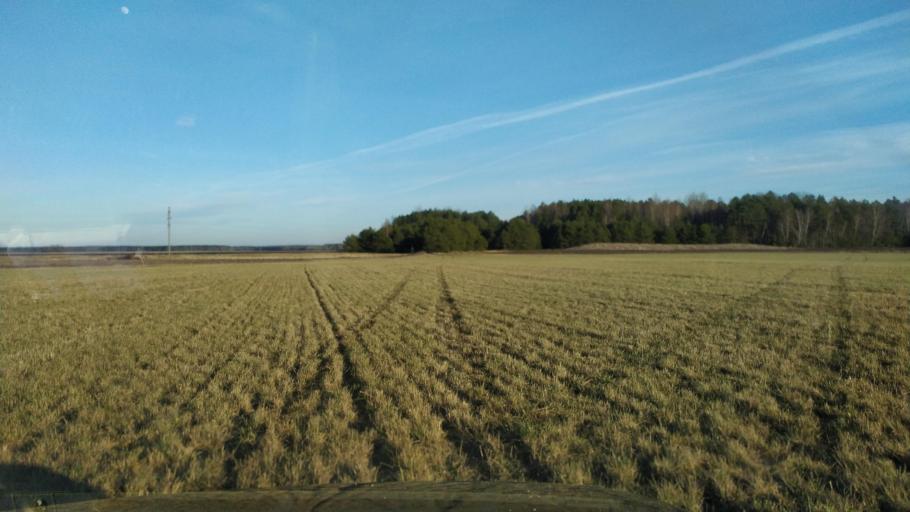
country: BY
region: Brest
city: Pruzhany
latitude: 52.5447
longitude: 24.3016
